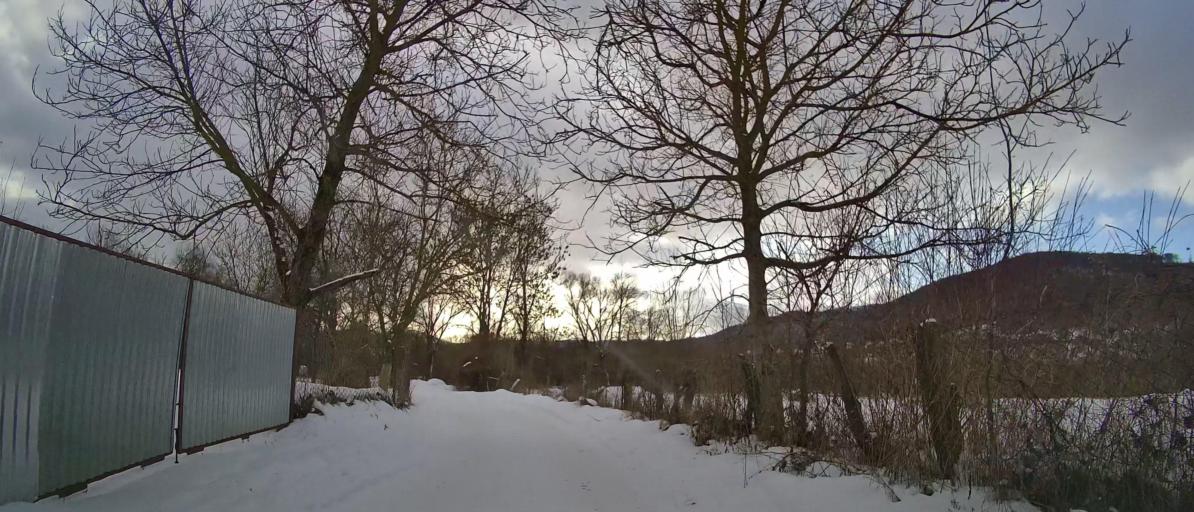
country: UA
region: Zakarpattia
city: Velykyi Bereznyi
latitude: 48.9123
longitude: 22.4646
